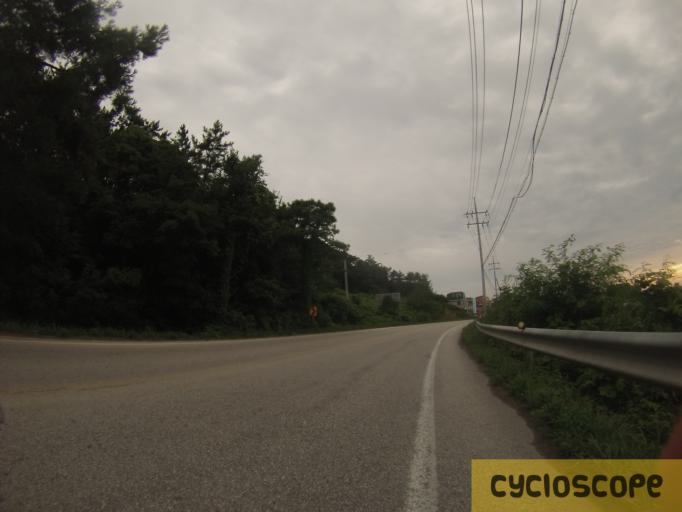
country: KR
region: Jeollabuk-do
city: Puan
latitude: 35.7567
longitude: 126.7686
